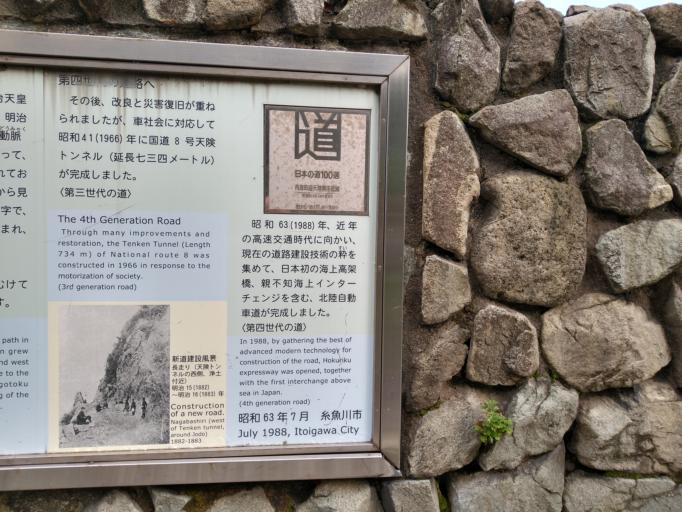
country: JP
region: Niigata
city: Itoigawa
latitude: 36.9931
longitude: 137.6970
